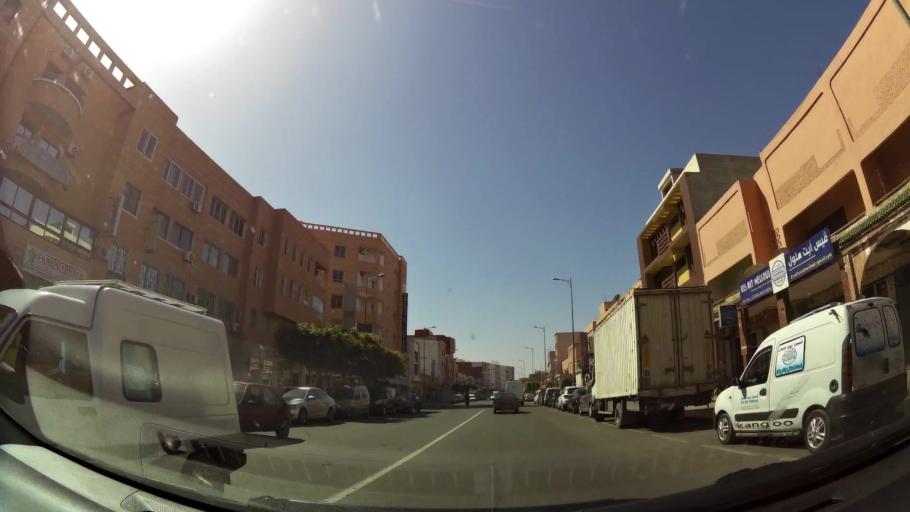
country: MA
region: Souss-Massa-Draa
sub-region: Inezgane-Ait Mellou
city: Inezgane
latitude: 30.3436
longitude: -9.5026
